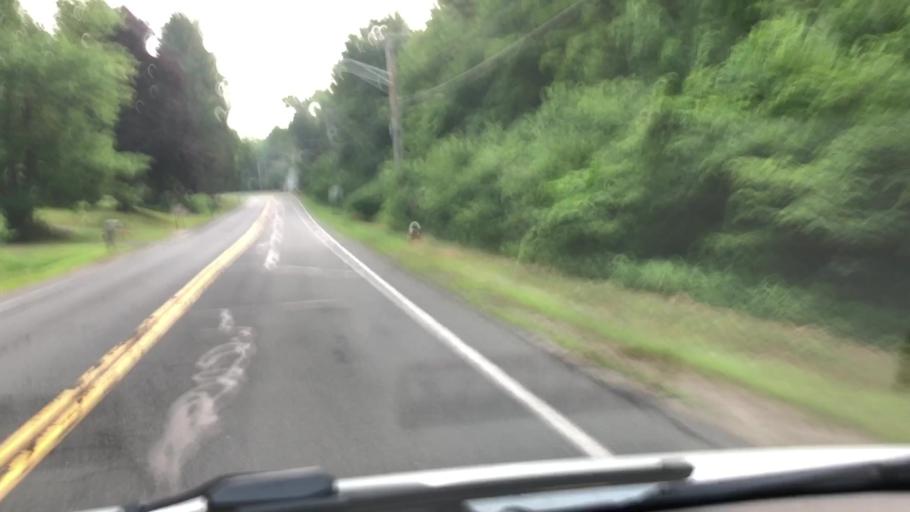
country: US
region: Massachusetts
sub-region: Hampshire County
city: Northampton
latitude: 42.3112
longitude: -72.6731
